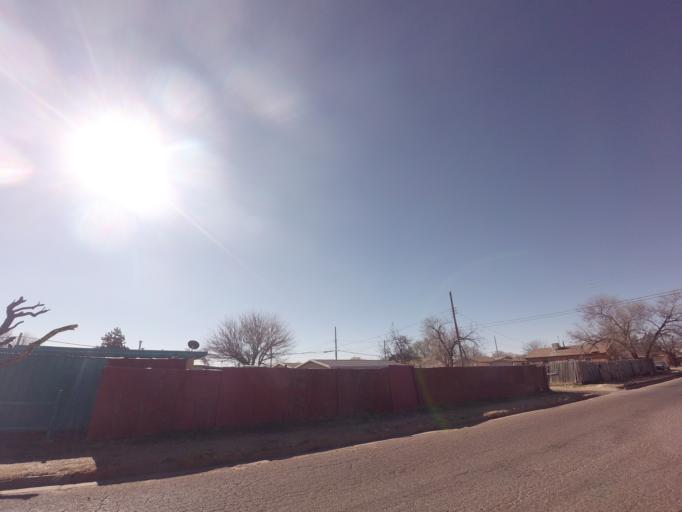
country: US
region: New Mexico
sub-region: Curry County
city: Clovis
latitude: 34.4083
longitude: -103.2254
